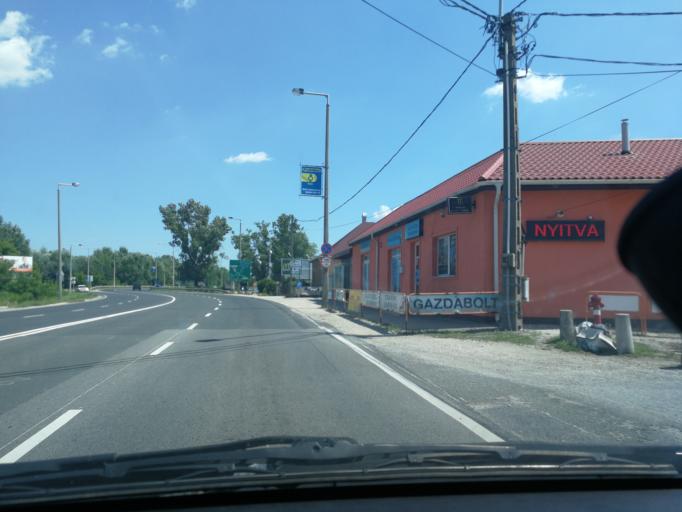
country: HU
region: Fejer
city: Szekesfehervar
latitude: 47.2059
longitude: 18.3834
